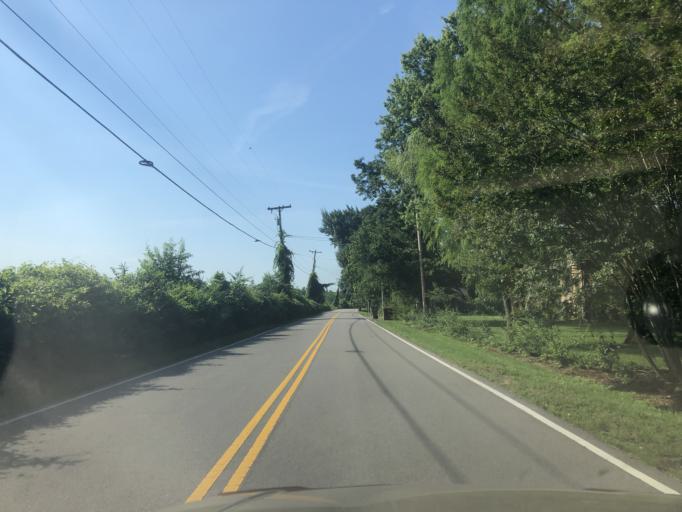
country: US
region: Tennessee
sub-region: Davidson County
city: Lakewood
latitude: 36.2277
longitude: -86.7079
